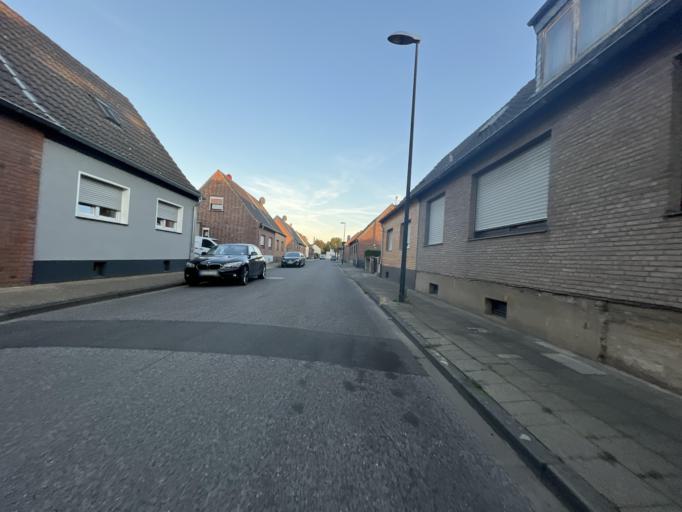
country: DE
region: North Rhine-Westphalia
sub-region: Regierungsbezirk Koln
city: Niederzier
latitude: 50.8501
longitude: 6.4269
